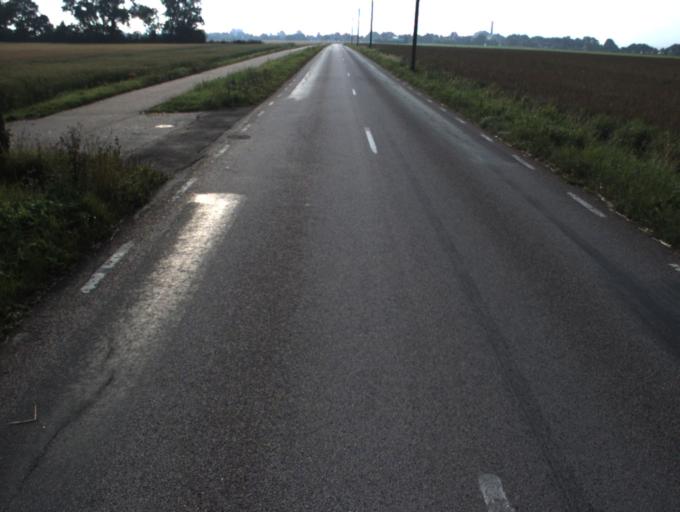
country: SE
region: Skane
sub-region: Angelholms Kommun
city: Strovelstorp
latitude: 56.1396
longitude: 12.7983
